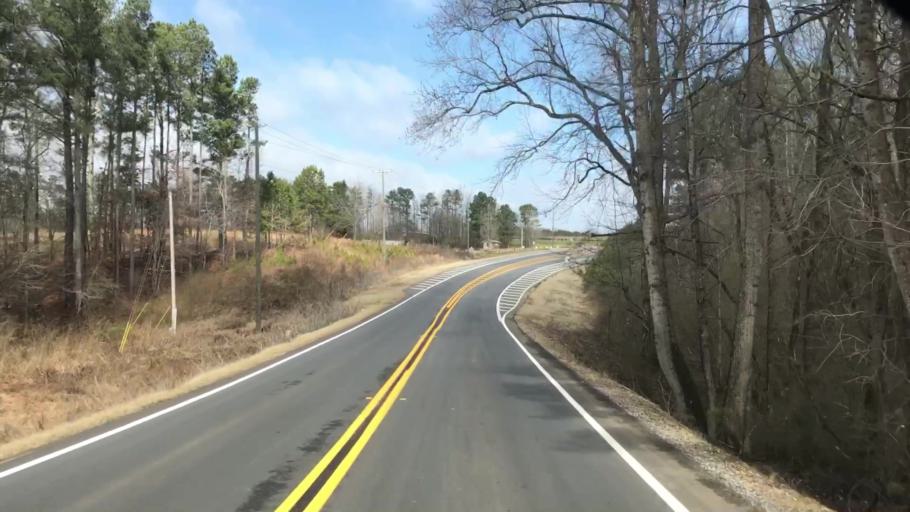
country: US
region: Georgia
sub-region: Hall County
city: Oakwood
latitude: 34.1637
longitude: -83.8356
